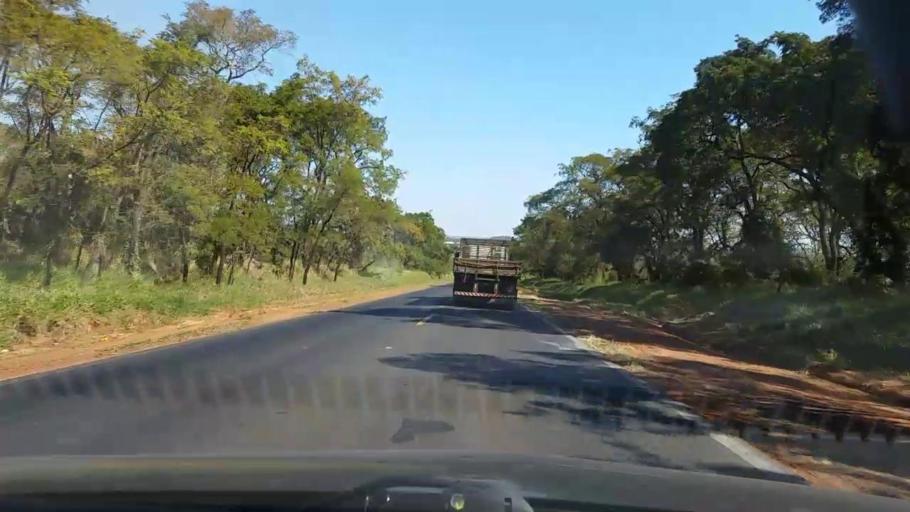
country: BR
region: Sao Paulo
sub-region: Sao Manuel
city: Sao Manuel
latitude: -22.7950
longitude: -48.6588
